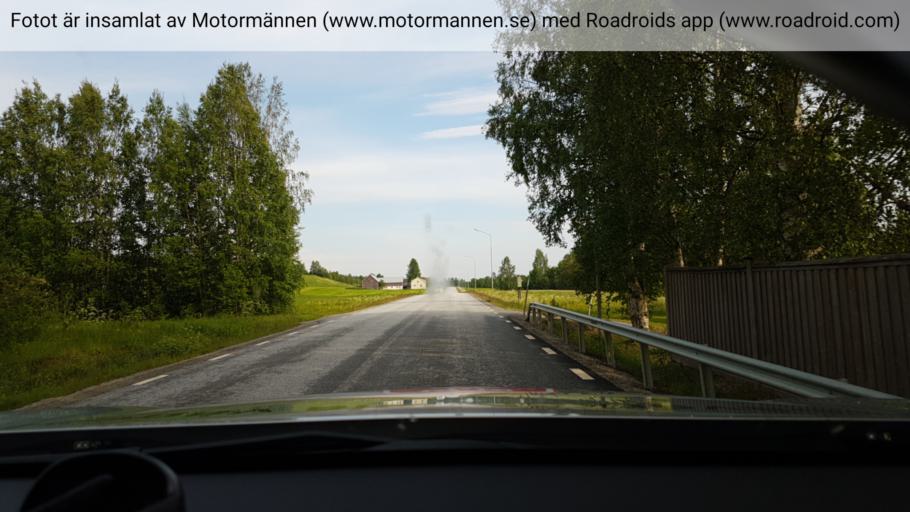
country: SE
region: Vaesterbotten
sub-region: Vindelns Kommun
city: Vindeln
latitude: 64.1738
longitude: 19.4852
